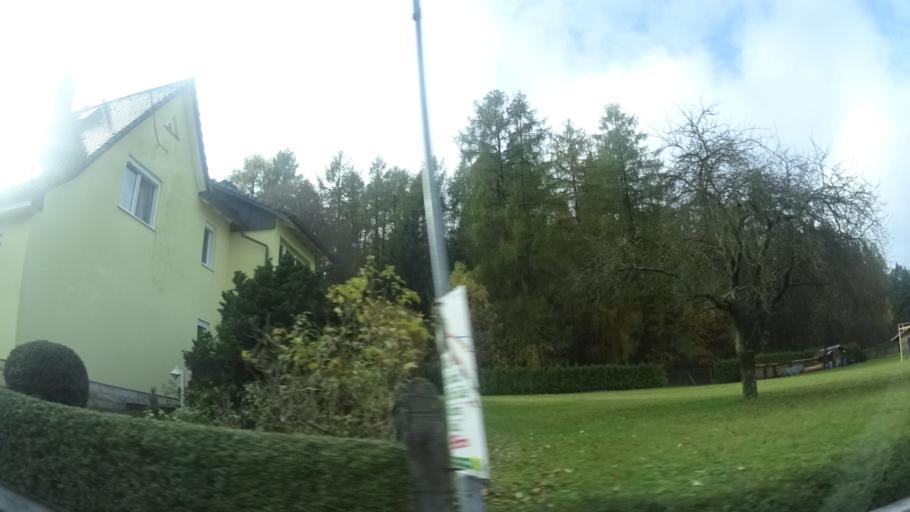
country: DE
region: Thuringia
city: Schleusingen
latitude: 50.4808
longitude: 10.8284
